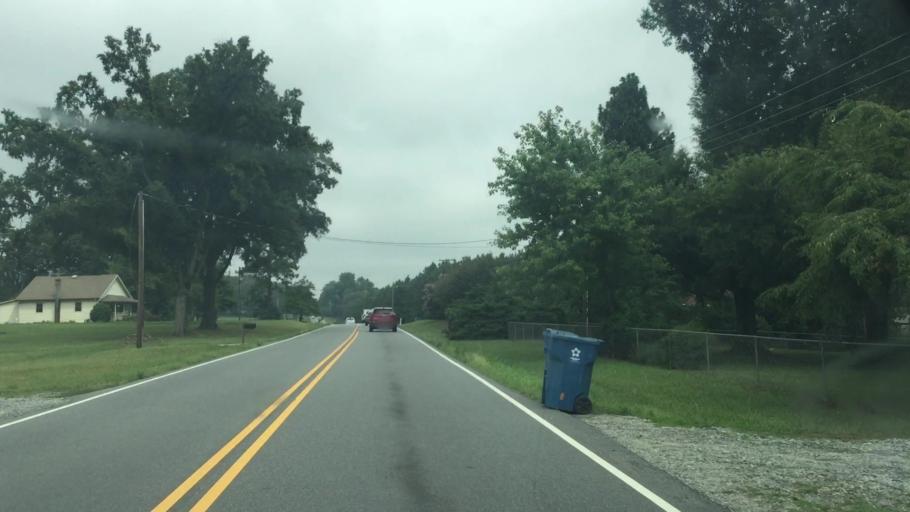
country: US
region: North Carolina
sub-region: Rowan County
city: Enochville
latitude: 35.4648
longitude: -80.7398
